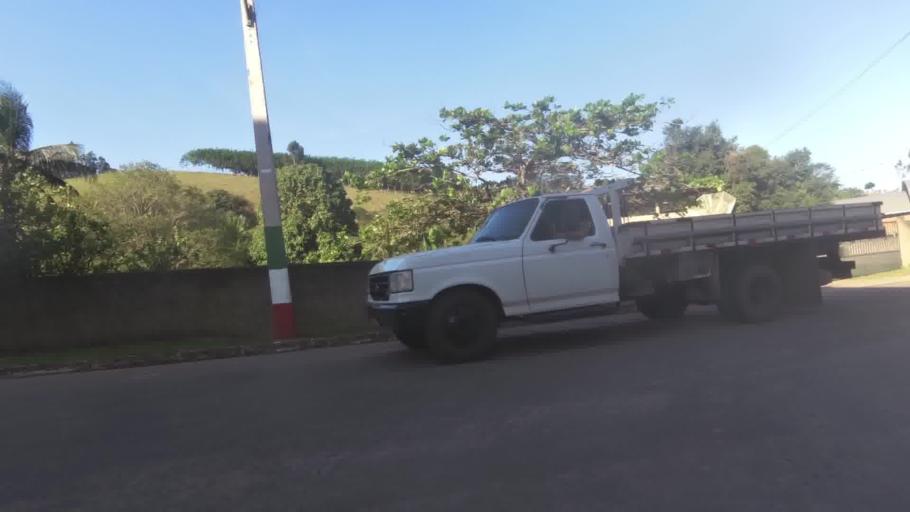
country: BR
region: Espirito Santo
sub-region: Iconha
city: Iconha
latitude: -20.7294
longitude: -40.7783
